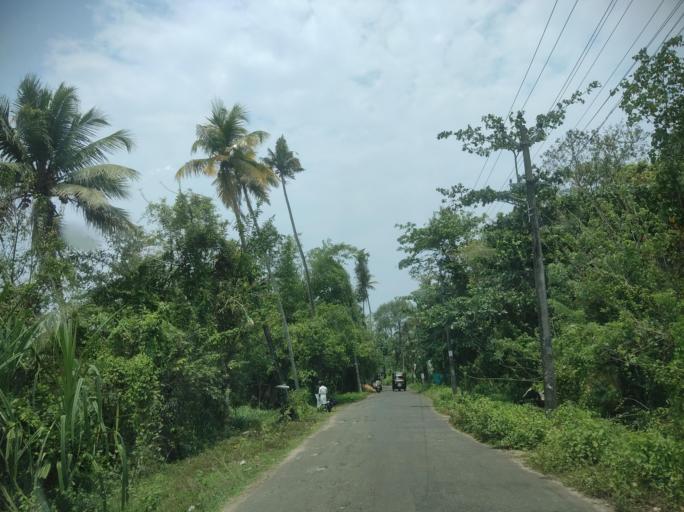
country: IN
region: Kerala
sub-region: Alappuzha
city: Vayalar
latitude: 9.7463
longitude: 76.3251
